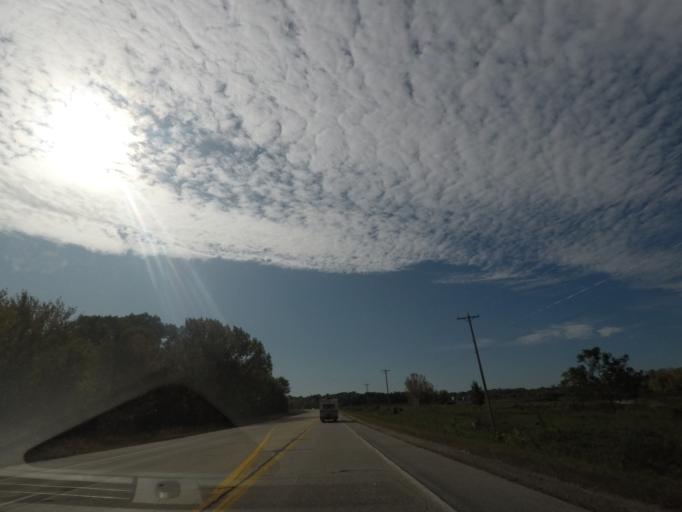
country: US
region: Iowa
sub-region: Story County
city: Ames
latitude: 42.0702
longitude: -93.6224
